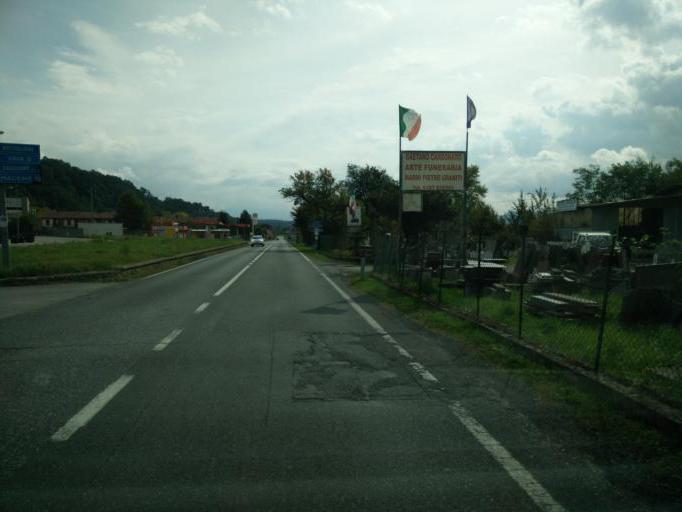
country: IT
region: Tuscany
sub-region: Provincia di Massa-Carrara
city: Pontremoli
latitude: 44.3620
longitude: 9.8976
